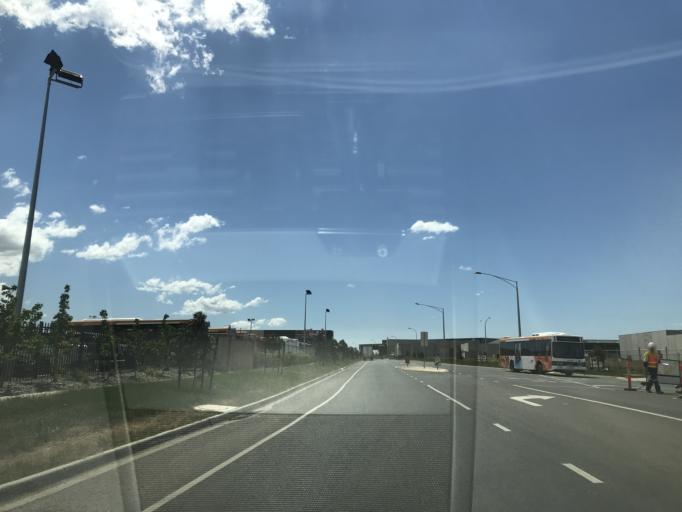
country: AU
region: Victoria
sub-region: Wyndham
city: Truganina
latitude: -37.8380
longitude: 144.7399
